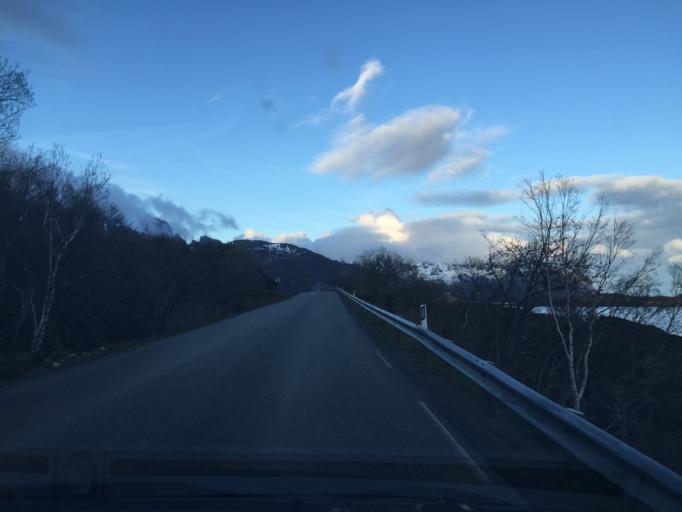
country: NO
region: Nordland
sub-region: Vagan
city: Svolvaer
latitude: 68.2841
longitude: 14.6636
